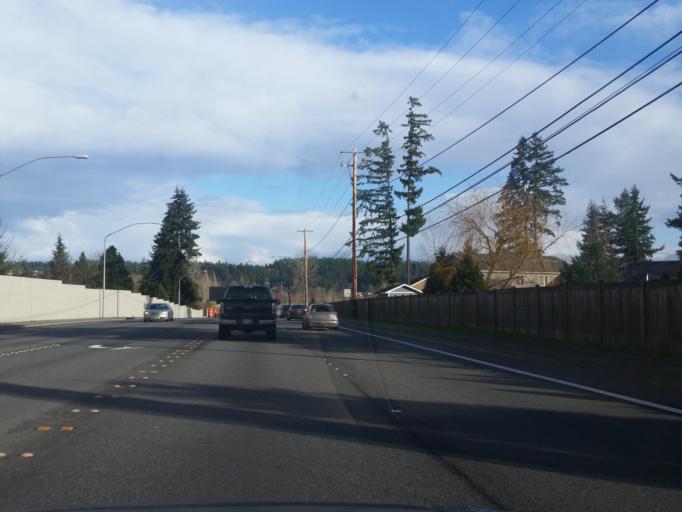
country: US
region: Washington
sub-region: Snohomish County
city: North Creek
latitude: 47.8094
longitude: -122.2200
